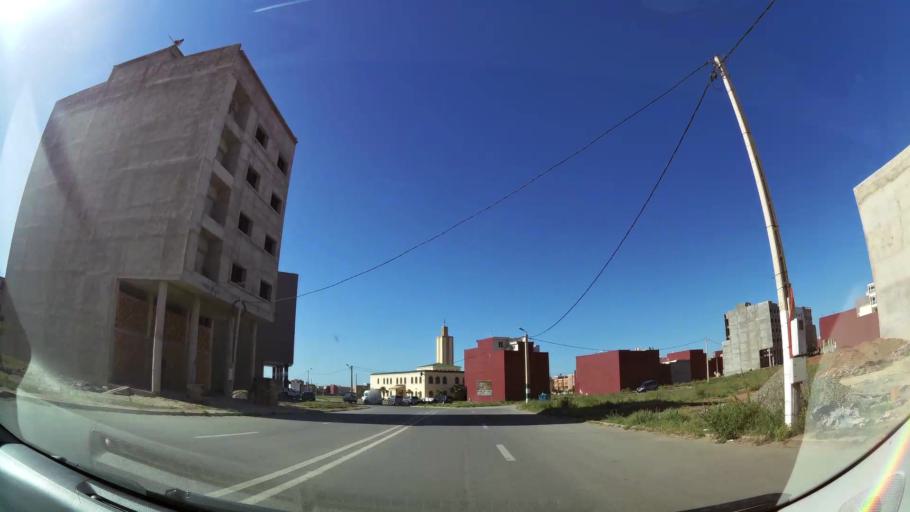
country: MA
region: Oriental
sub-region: Berkane-Taourirt
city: Berkane
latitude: 34.9398
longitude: -2.3345
